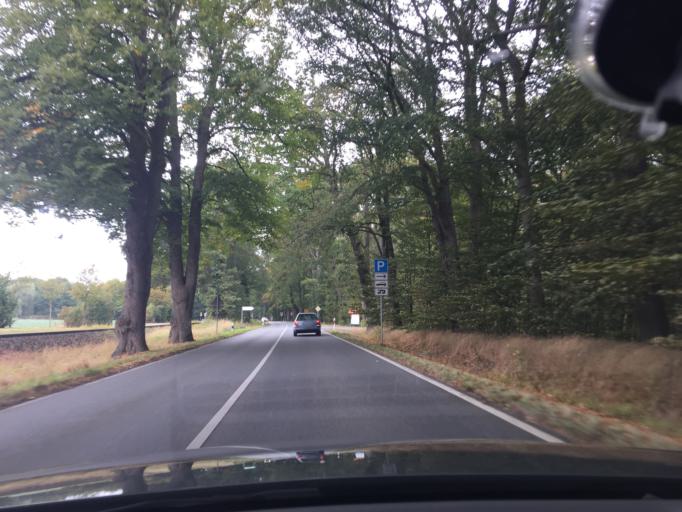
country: DE
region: Mecklenburg-Vorpommern
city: Bad Doberan
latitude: 54.1380
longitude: 11.8524
